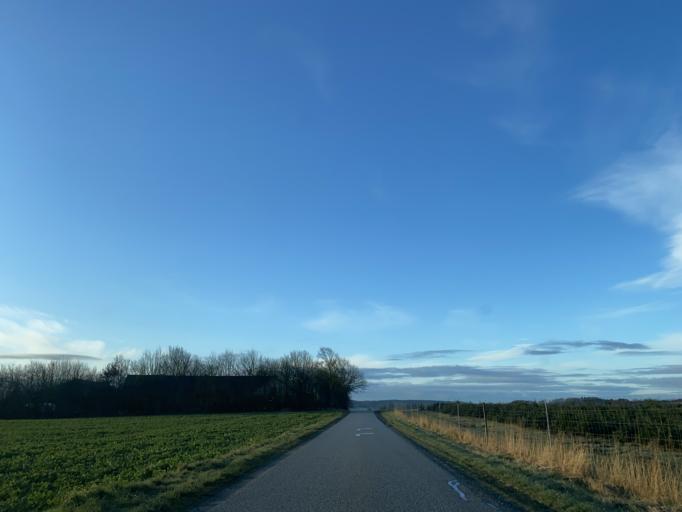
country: DK
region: Central Jutland
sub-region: Favrskov Kommune
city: Hammel
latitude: 56.2429
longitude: 9.7394
